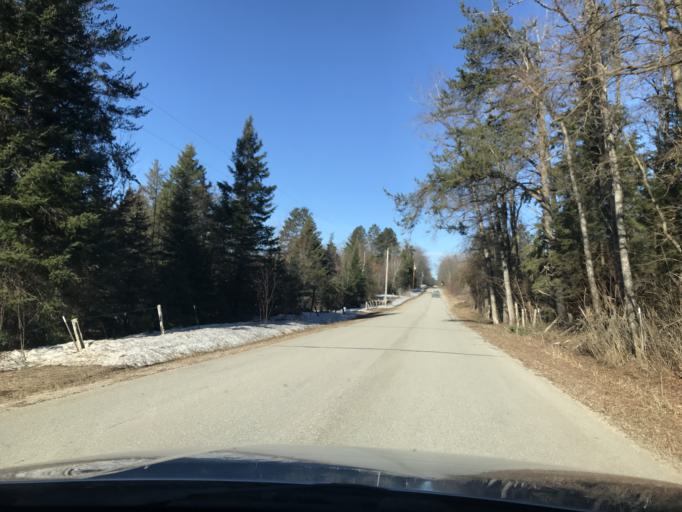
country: US
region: Wisconsin
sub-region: Marinette County
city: Niagara
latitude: 45.3901
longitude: -88.0654
